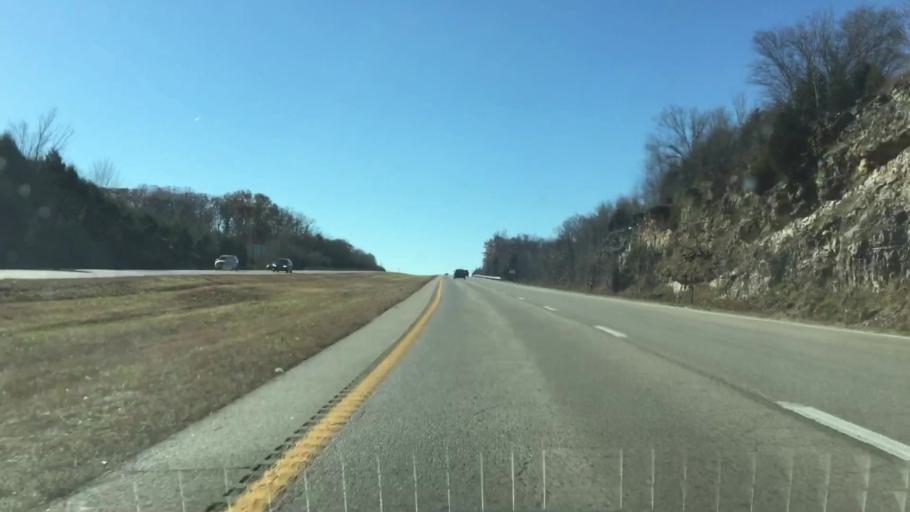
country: US
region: Missouri
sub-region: Cole County
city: Wardsville
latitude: 38.5011
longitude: -92.2671
